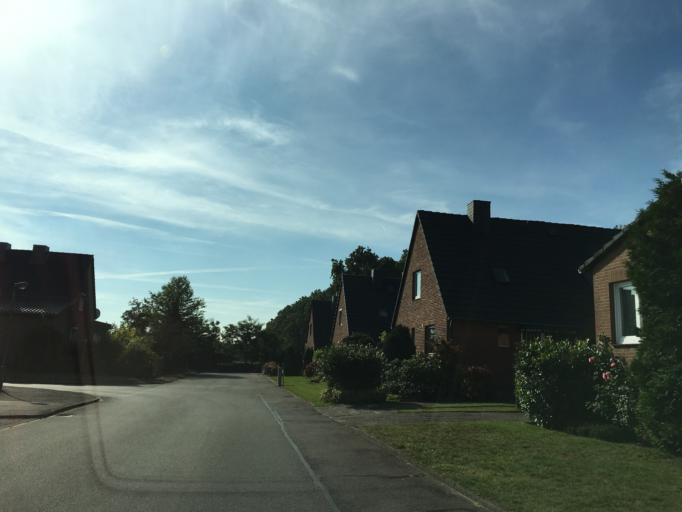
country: DE
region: Lower Saxony
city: Adendorf
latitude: 53.2785
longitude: 10.4626
